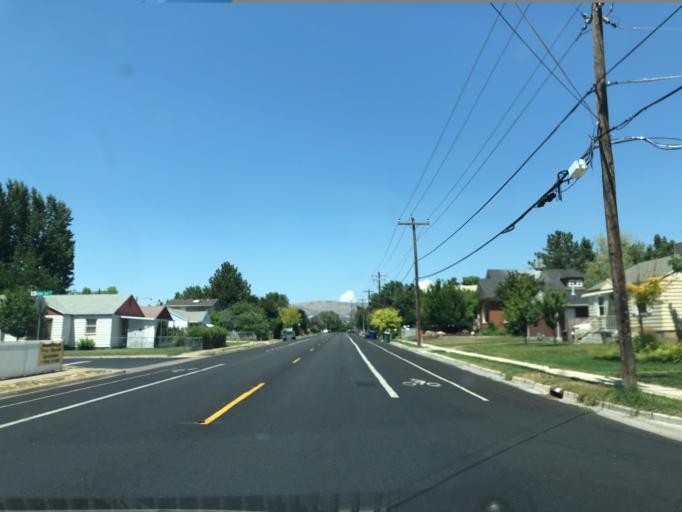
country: US
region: Utah
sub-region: Salt Lake County
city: South Salt Lake
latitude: 40.7191
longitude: -111.8769
